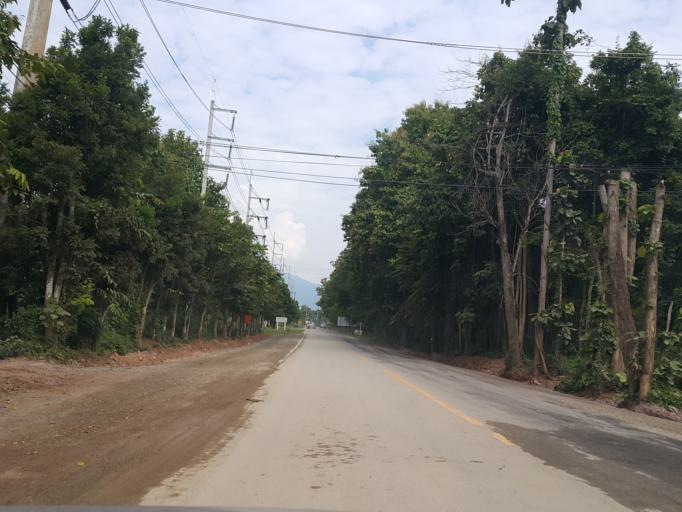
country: TH
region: Mae Hong Son
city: Mae Hong Son
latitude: 19.3434
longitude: 97.9638
